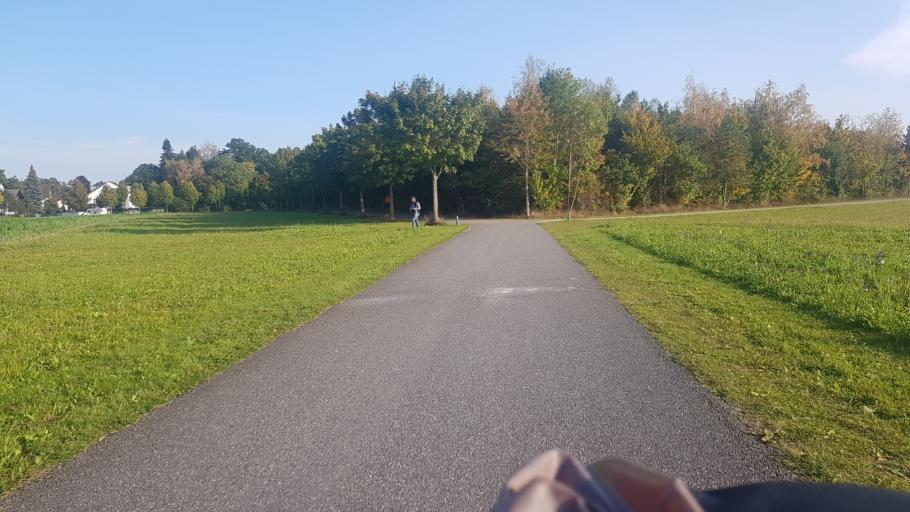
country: DE
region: Bavaria
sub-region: Upper Bavaria
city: Neubiberg
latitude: 48.0894
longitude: 11.6590
